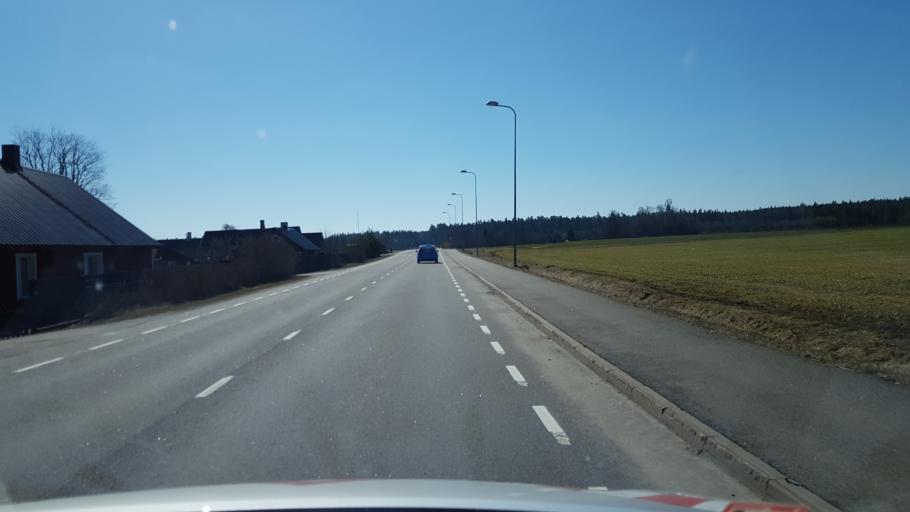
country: EE
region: Laeaene-Virumaa
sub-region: Vinni vald
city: Vinni
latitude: 59.1472
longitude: 26.5947
